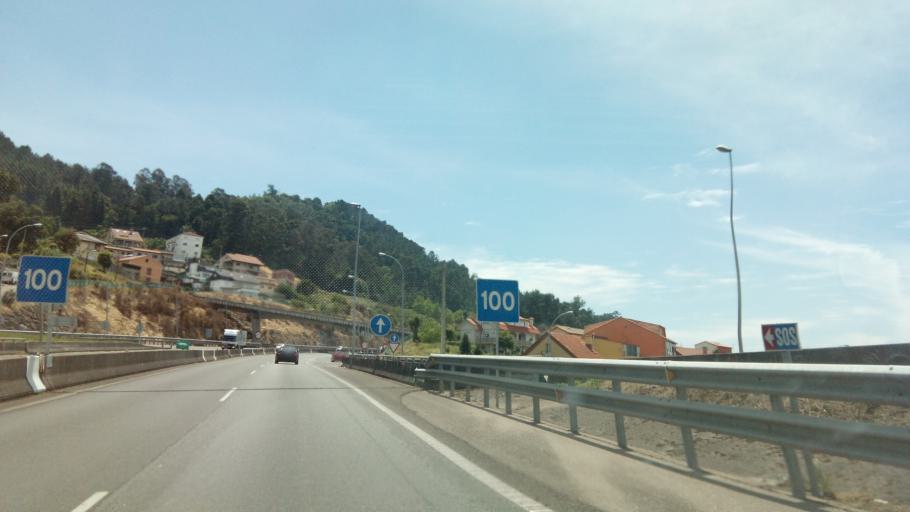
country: ES
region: Galicia
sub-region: Provincia de Pontevedra
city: Vigo
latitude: 42.2580
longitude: -8.6752
